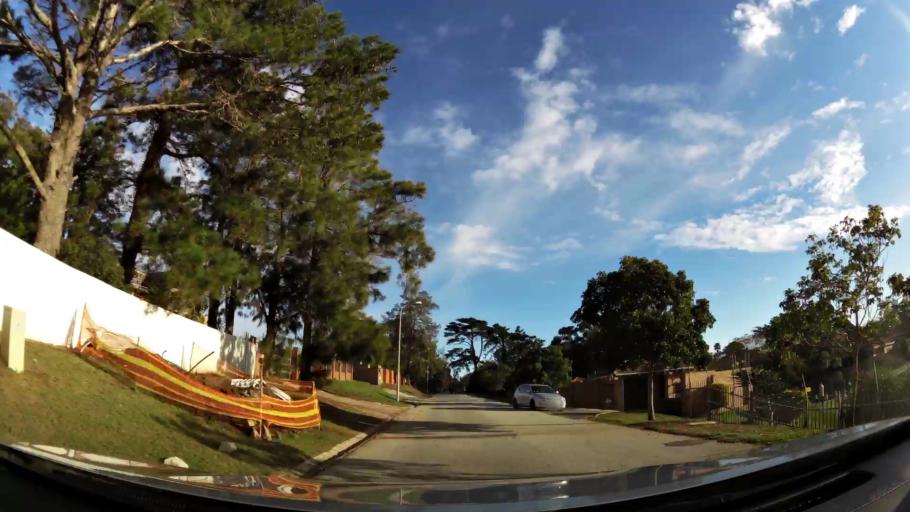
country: ZA
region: Eastern Cape
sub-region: Nelson Mandela Bay Metropolitan Municipality
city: Port Elizabeth
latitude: -33.9638
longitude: 25.5076
